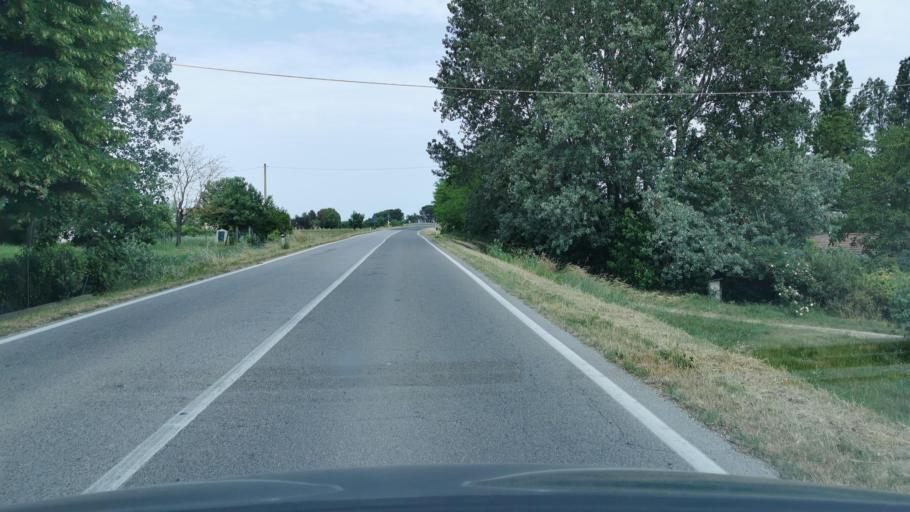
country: IT
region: Emilia-Romagna
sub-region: Provincia di Ravenna
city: Sant'Alberto
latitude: 44.5366
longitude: 12.1281
